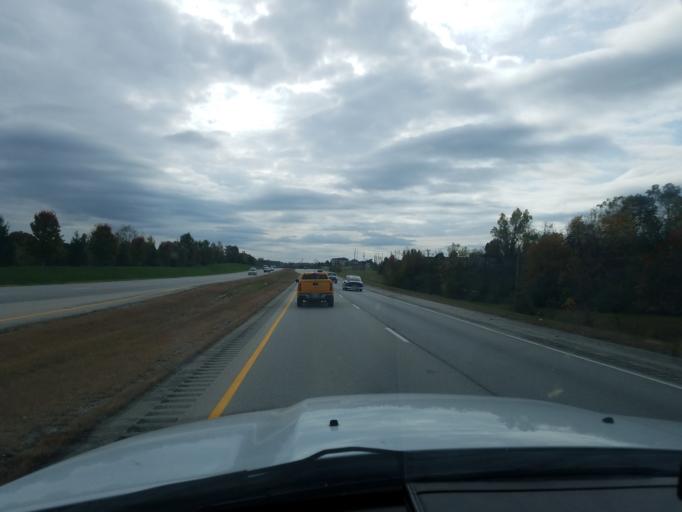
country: US
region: Kentucky
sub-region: Jefferson County
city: Fern Creek
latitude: 38.1244
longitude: -85.5742
